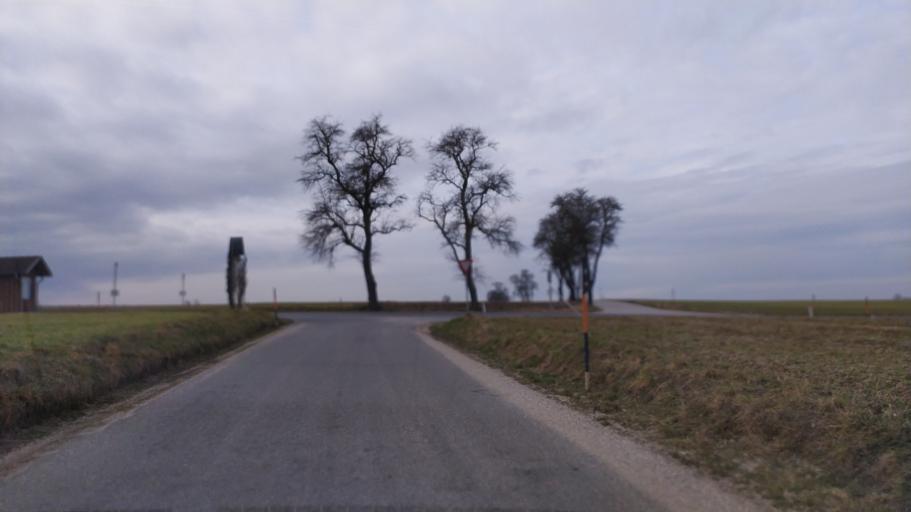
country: AT
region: Lower Austria
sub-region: Politischer Bezirk Amstetten
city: Strengberg
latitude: 48.1473
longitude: 14.6986
